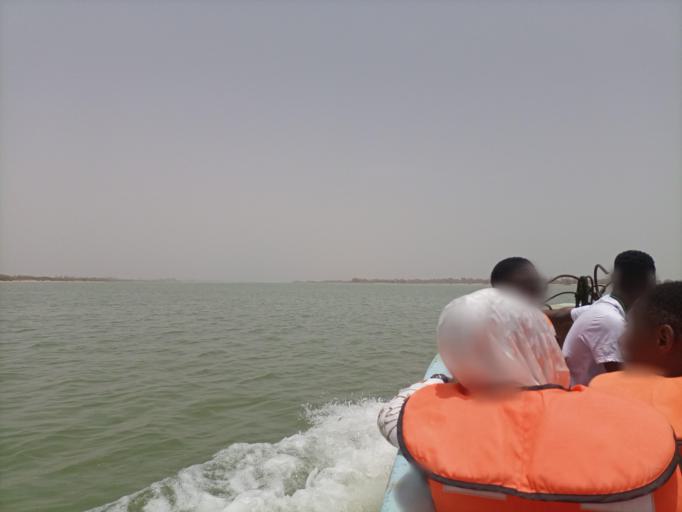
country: SN
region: Saint-Louis
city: Saint-Louis
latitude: 15.8622
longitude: -16.5155
